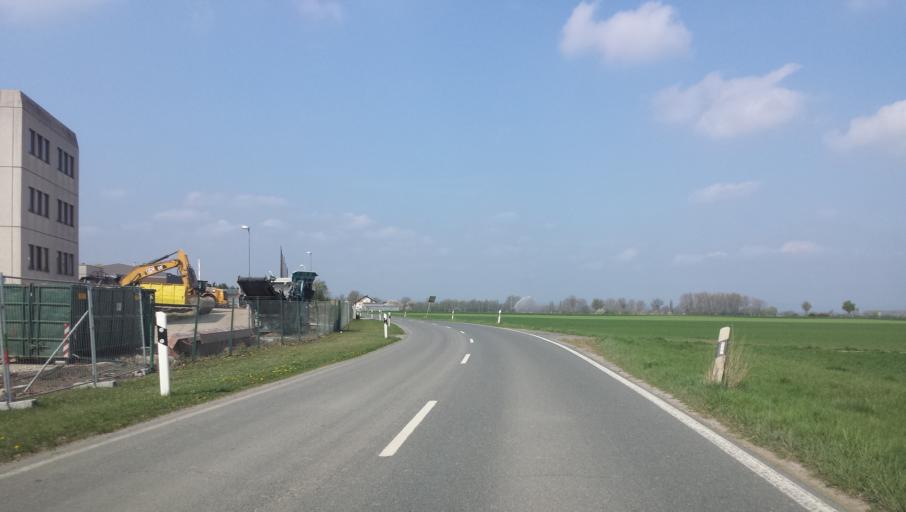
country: DE
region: Hesse
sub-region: Regierungsbezirk Darmstadt
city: Trebur
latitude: 49.8927
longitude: 8.4052
